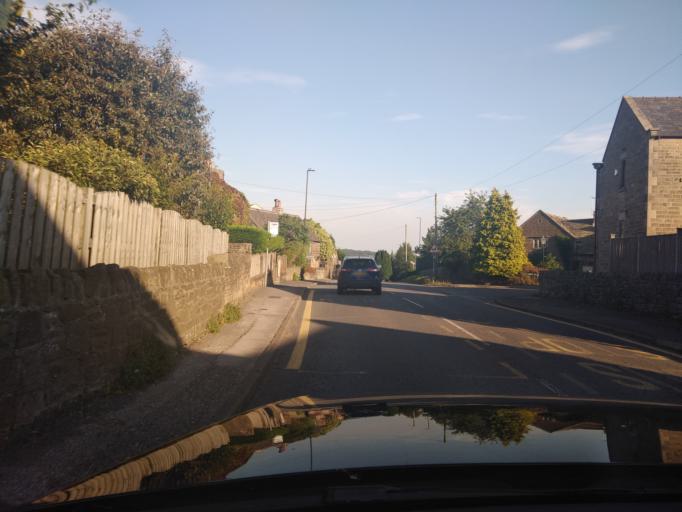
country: GB
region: England
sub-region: Derbyshire
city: Dronfield
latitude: 53.3033
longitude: -1.5063
